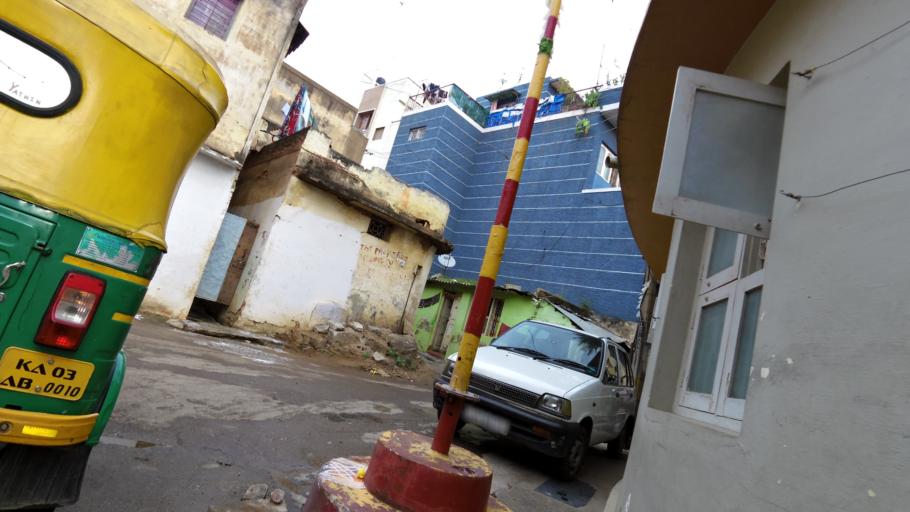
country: IN
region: Karnataka
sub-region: Bangalore Urban
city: Bangalore
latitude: 12.9960
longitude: 77.6283
